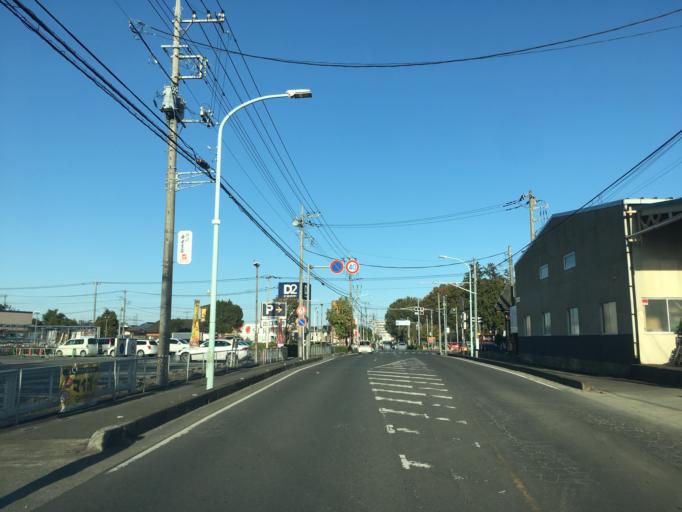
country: JP
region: Saitama
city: Tokorozawa
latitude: 35.8082
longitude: 139.4923
